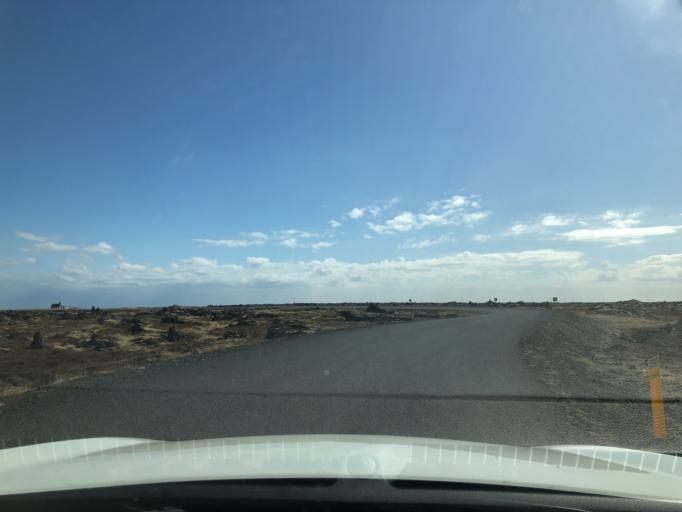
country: IS
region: West
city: Olafsvik
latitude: 64.8262
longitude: -23.3943
